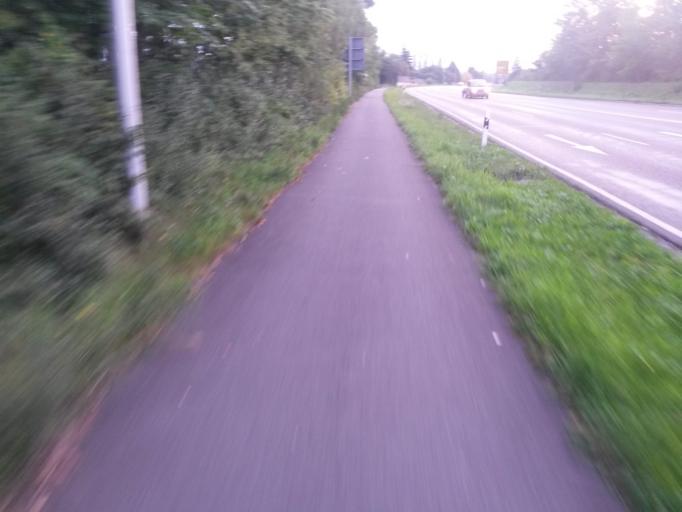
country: DE
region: Bavaria
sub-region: Regierungsbezirk Mittelfranken
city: Zirndorf
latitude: 49.4328
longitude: 10.9408
